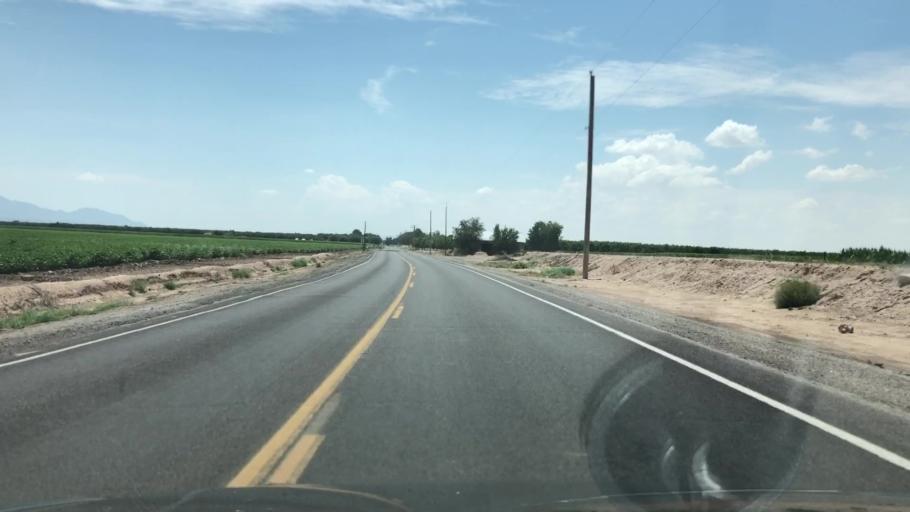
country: US
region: New Mexico
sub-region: Dona Ana County
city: Berino
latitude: 32.0257
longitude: -106.6718
